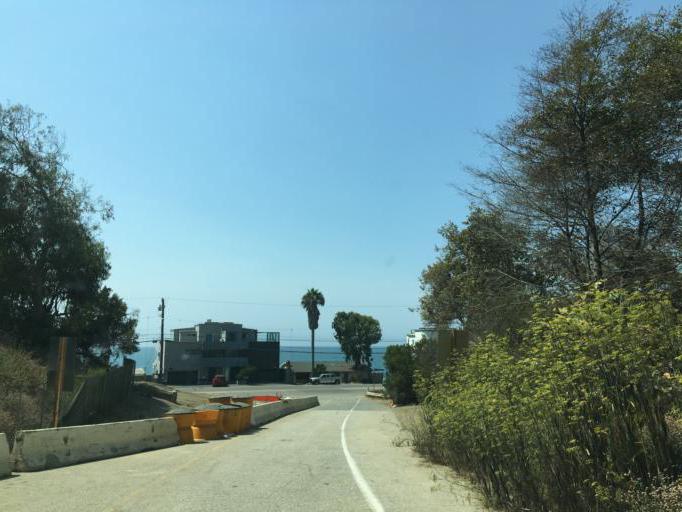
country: US
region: California
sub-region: Los Angeles County
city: Las Flores
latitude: 34.0402
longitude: -118.5890
